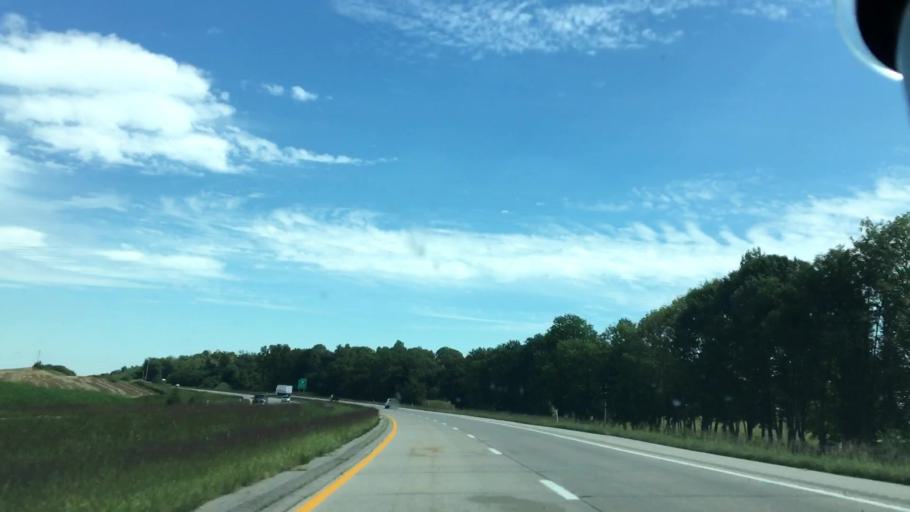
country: US
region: Kentucky
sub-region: Daviess County
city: Owensboro
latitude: 37.7514
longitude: -87.2882
